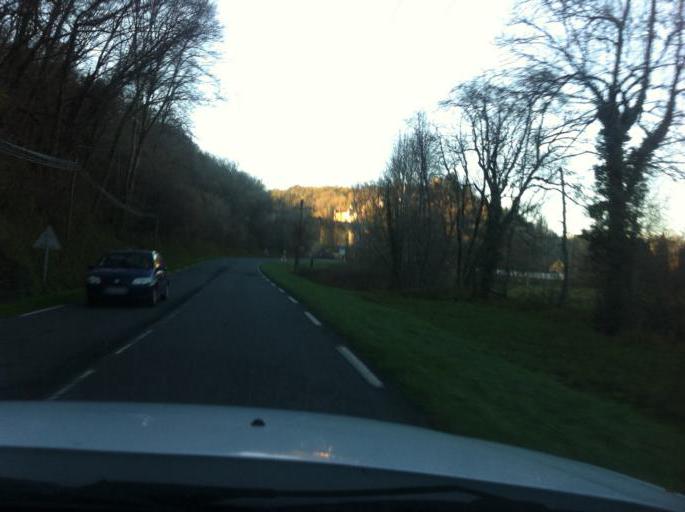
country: FR
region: Aquitaine
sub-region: Departement de la Dordogne
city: Sarlat-la-Caneda
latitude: 44.9129
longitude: 1.1570
